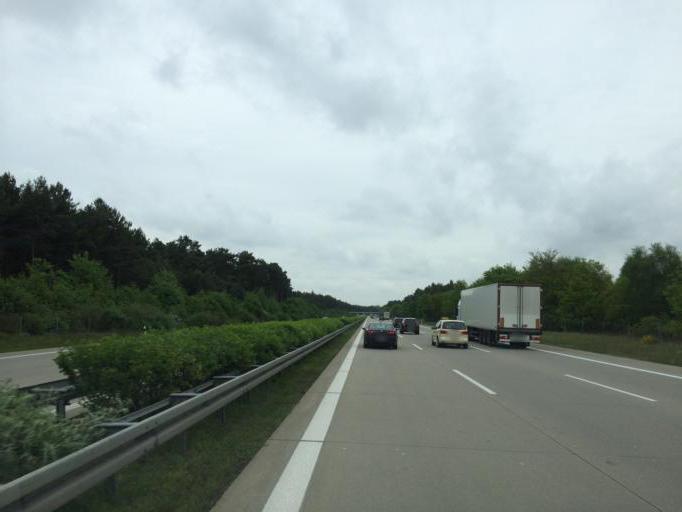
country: DE
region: Brandenburg
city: Wollin
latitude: 52.3270
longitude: 12.4984
